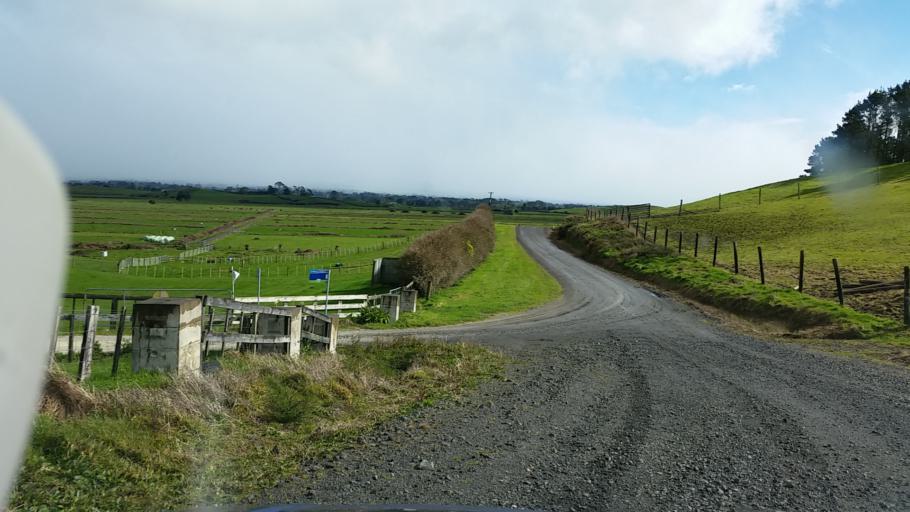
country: NZ
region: Taranaki
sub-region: South Taranaki District
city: Eltham
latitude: -39.2835
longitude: 174.3103
